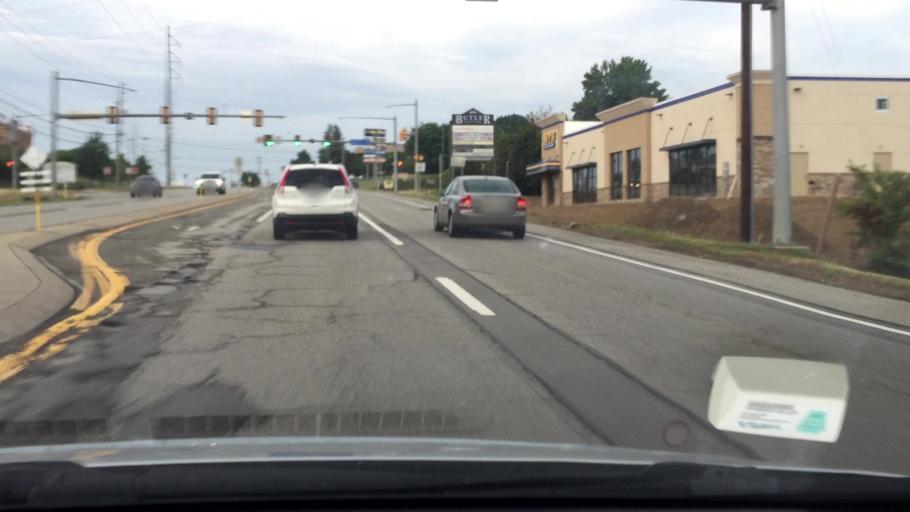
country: US
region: Pennsylvania
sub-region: Butler County
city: Cranberry Township
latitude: 40.6967
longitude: -80.1046
